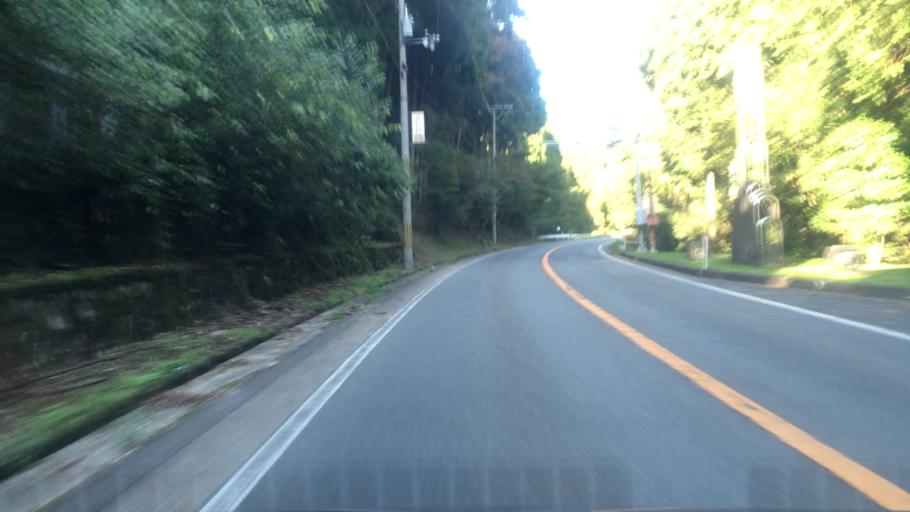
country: JP
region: Hyogo
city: Toyooka
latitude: 35.5806
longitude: 134.8571
